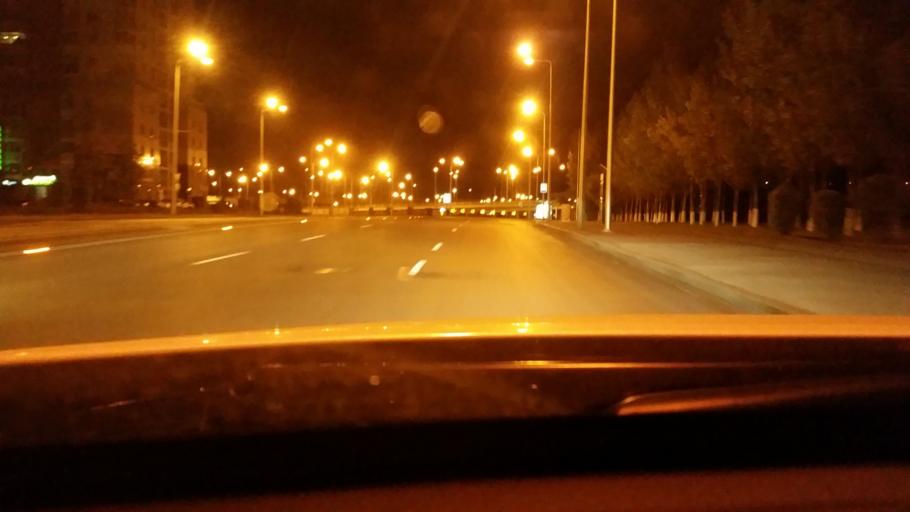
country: KZ
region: Astana Qalasy
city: Astana
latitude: 51.1296
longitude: 71.4396
